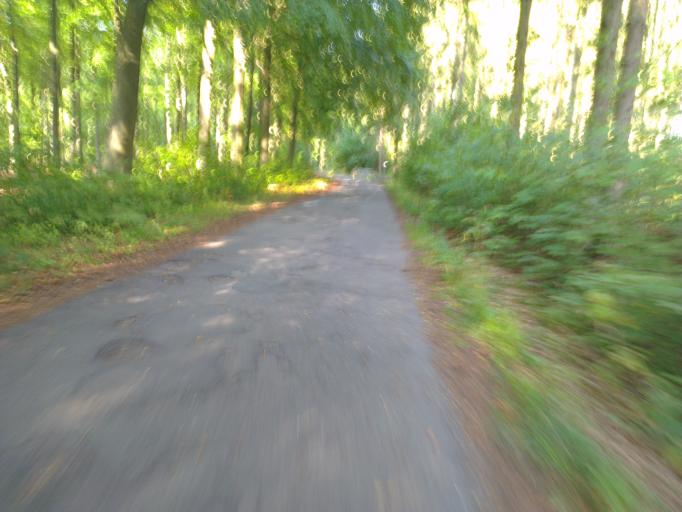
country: DK
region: Capital Region
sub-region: Frederikssund Kommune
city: Jaegerspris
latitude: 55.8800
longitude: 11.9915
